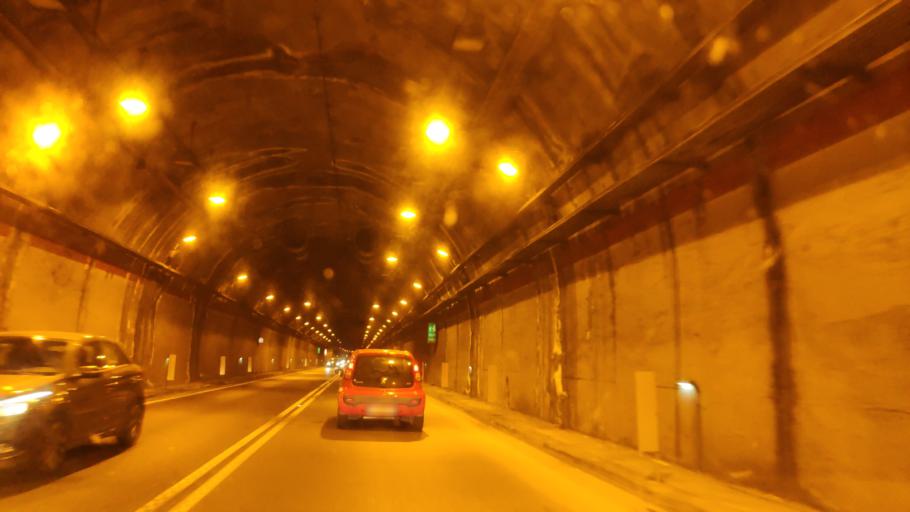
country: IT
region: Campania
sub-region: Provincia di Napoli
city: Castellammare di Stabia
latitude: 40.6881
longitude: 14.4636
